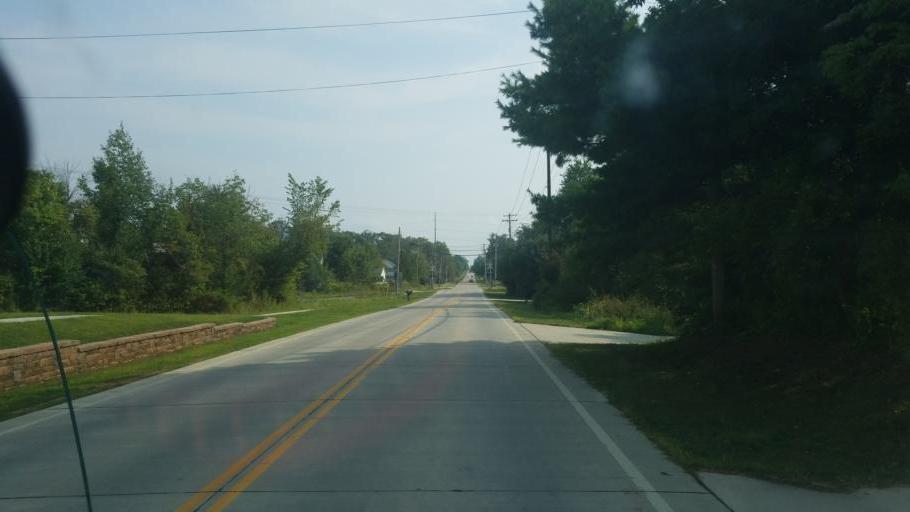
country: US
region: Ohio
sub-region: Medina County
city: Medina
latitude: 41.1225
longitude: -81.8840
